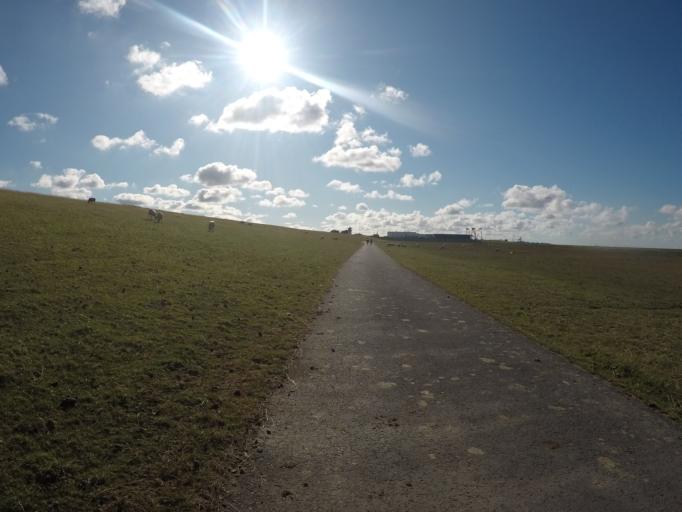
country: DE
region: Lower Saxony
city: Nordleda
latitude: 53.8346
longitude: 8.7787
